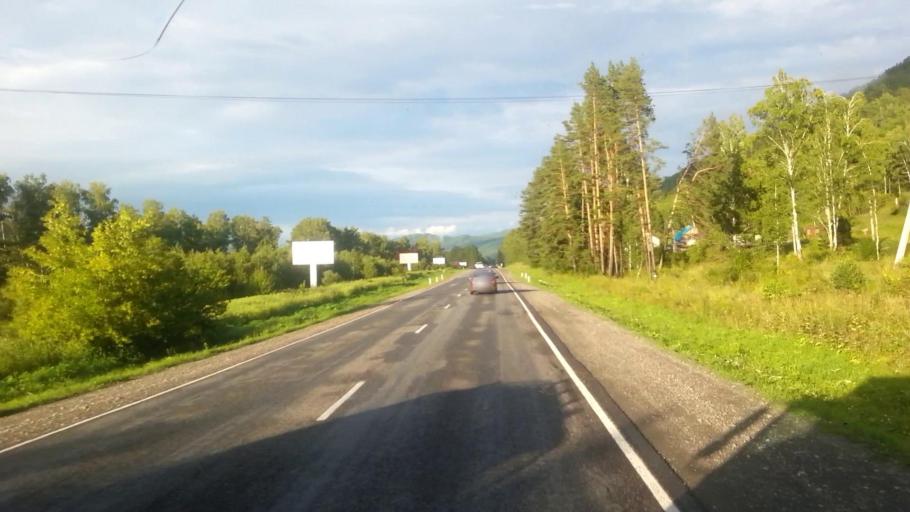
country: RU
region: Altay
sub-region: Mayminskiy Rayon
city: Manzherok
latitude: 51.8709
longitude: 85.7872
